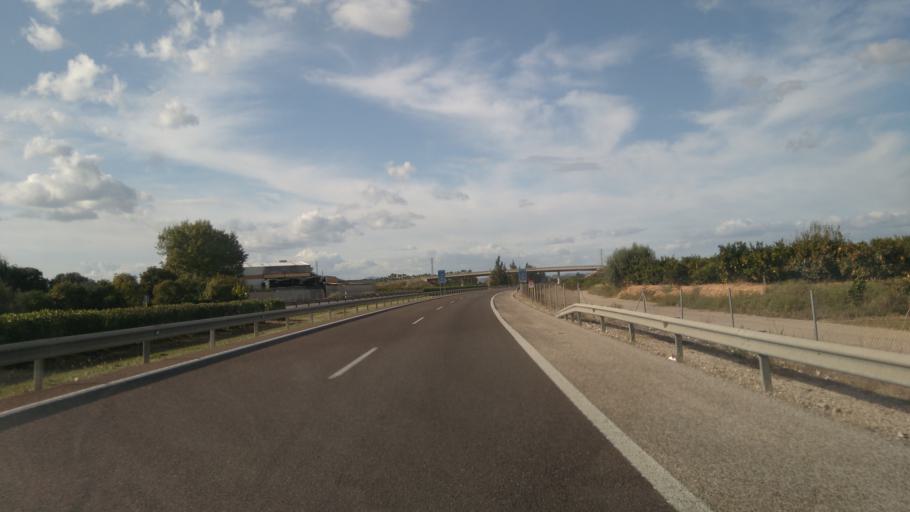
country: ES
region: Valencia
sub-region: Provincia de Valencia
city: Guadassuar
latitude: 39.1806
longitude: -0.4856
